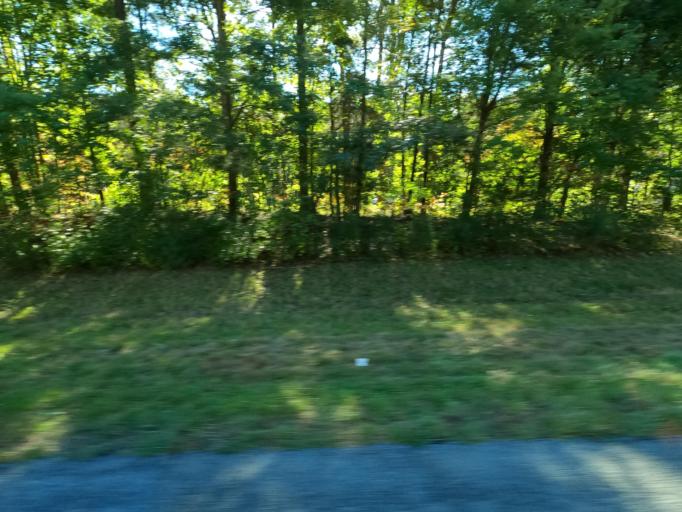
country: US
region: Tennessee
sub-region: Williamson County
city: Fairview
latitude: 36.0338
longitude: -87.1656
